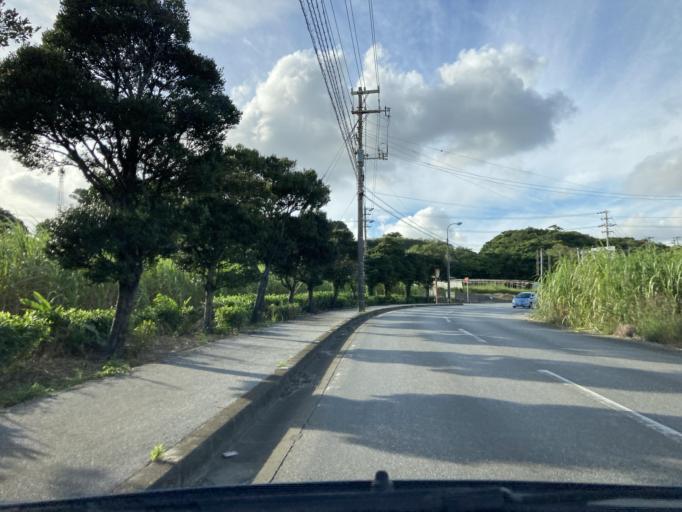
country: JP
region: Okinawa
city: Itoman
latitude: 26.1360
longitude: 127.7469
